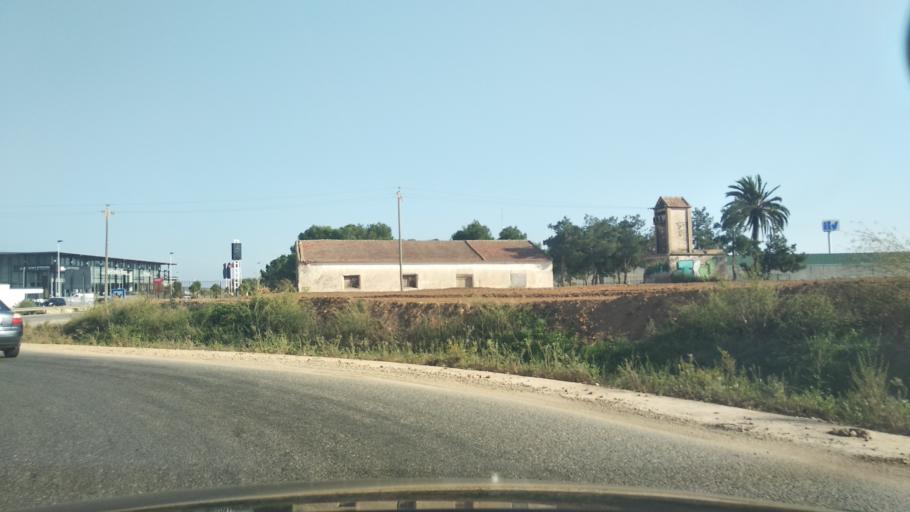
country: ES
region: Murcia
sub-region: Murcia
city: San Javier
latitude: 37.8135
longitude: -0.8408
